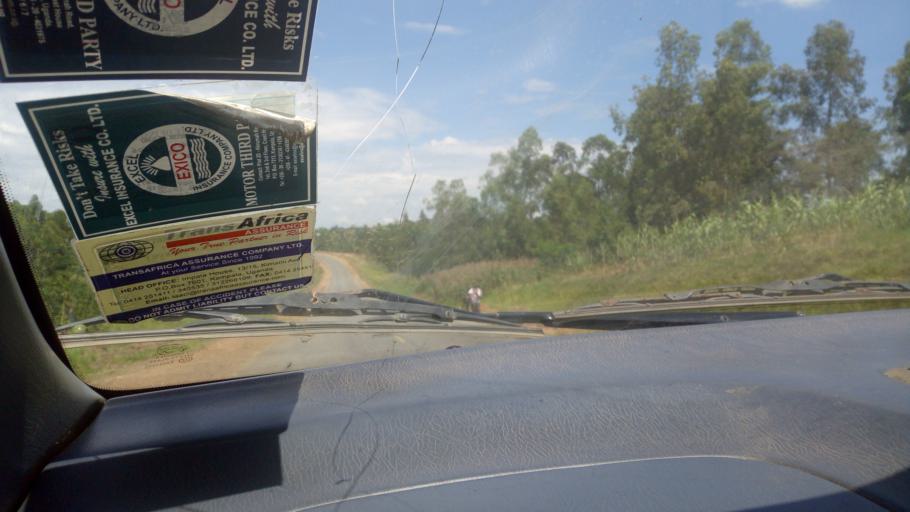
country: UG
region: Western Region
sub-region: Buhweju District
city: Buhweju
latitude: -0.2710
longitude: 30.5625
